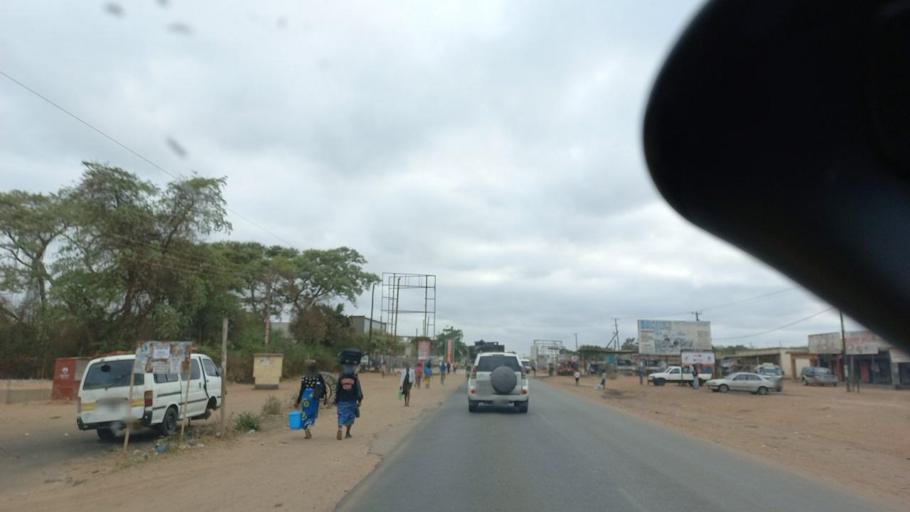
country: ZM
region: Lusaka
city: Chongwe
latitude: -15.3330
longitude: 28.6732
